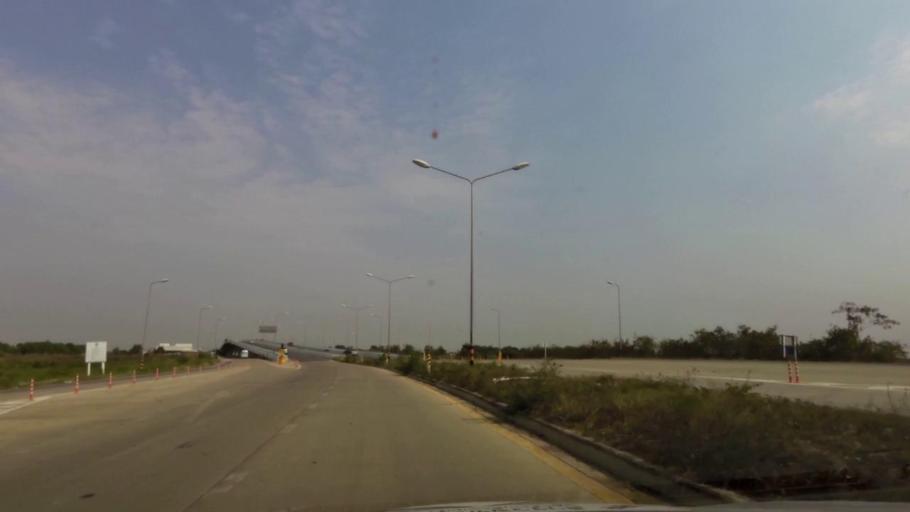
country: TH
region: Phra Nakhon Si Ayutthaya
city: Phra Nakhon Si Ayutthaya
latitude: 14.3303
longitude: 100.5796
